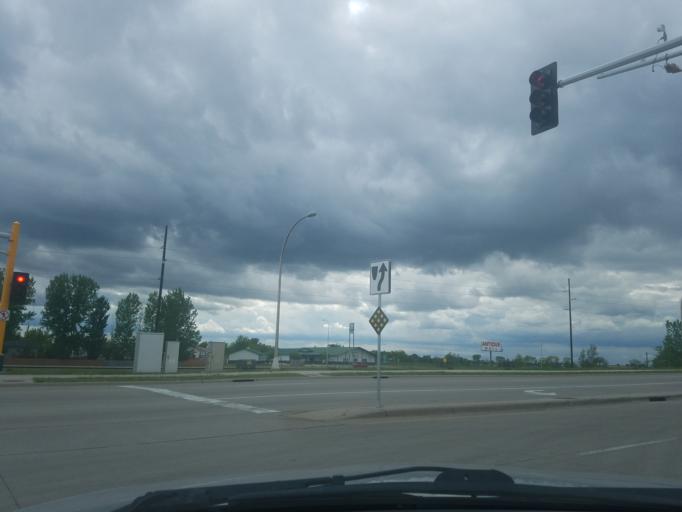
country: US
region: Minnesota
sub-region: Clay County
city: Dilworth
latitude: 46.8454
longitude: -96.7192
